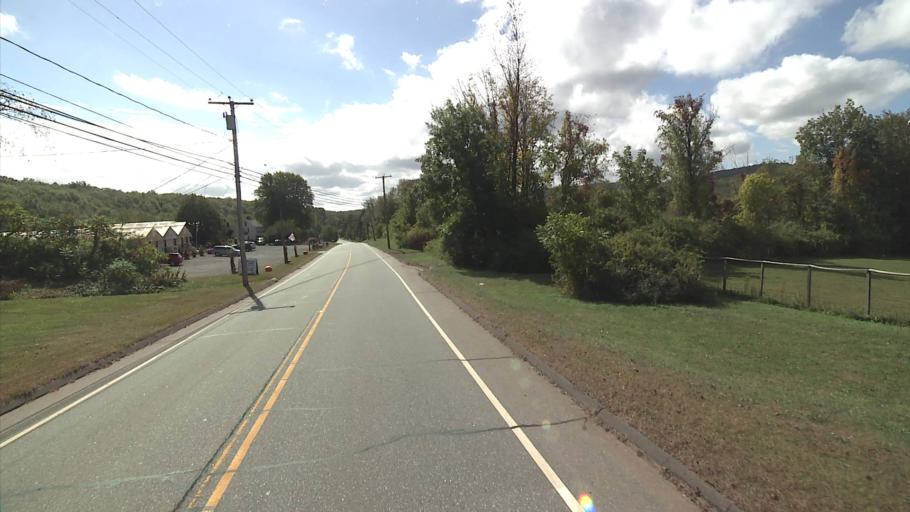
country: US
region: Connecticut
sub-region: Middlesex County
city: Durham
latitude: 41.5251
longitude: -72.7291
